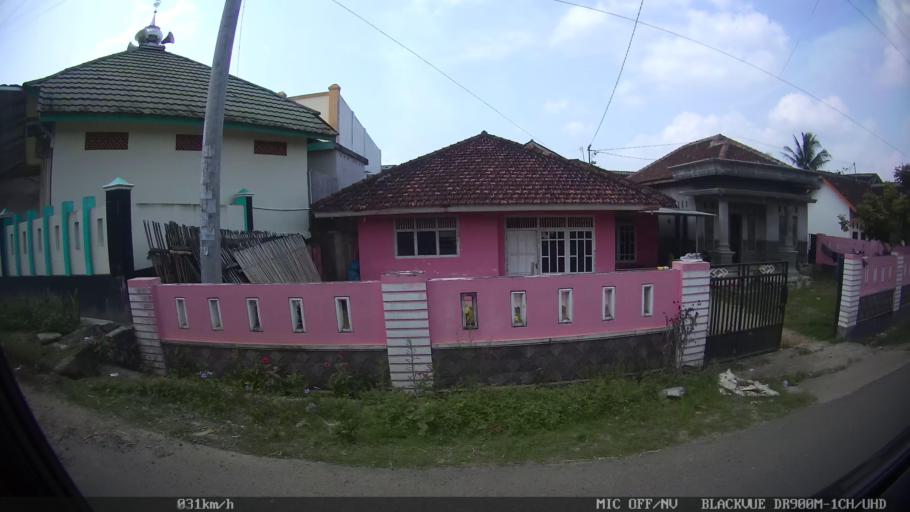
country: ID
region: Lampung
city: Pringsewu
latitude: -5.3601
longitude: 104.9683
